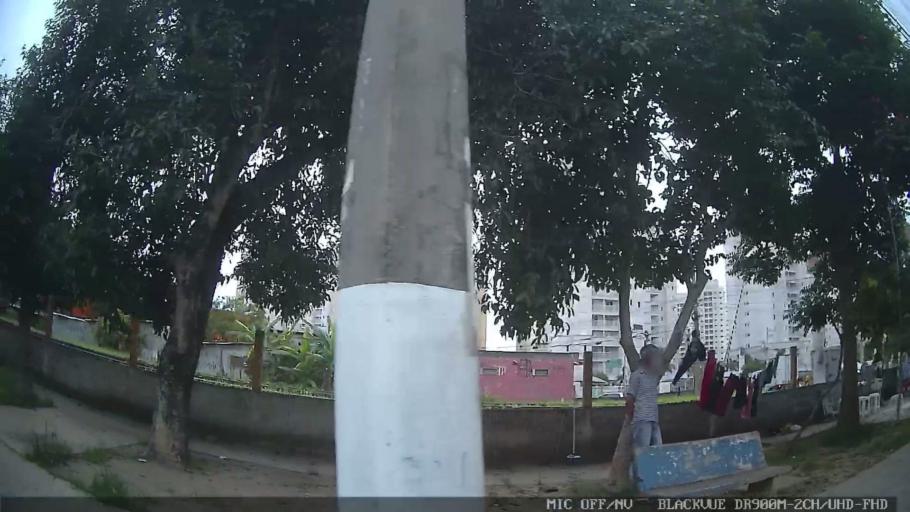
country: BR
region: Sao Paulo
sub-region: Mogi das Cruzes
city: Mogi das Cruzes
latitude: -23.5050
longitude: -46.1517
